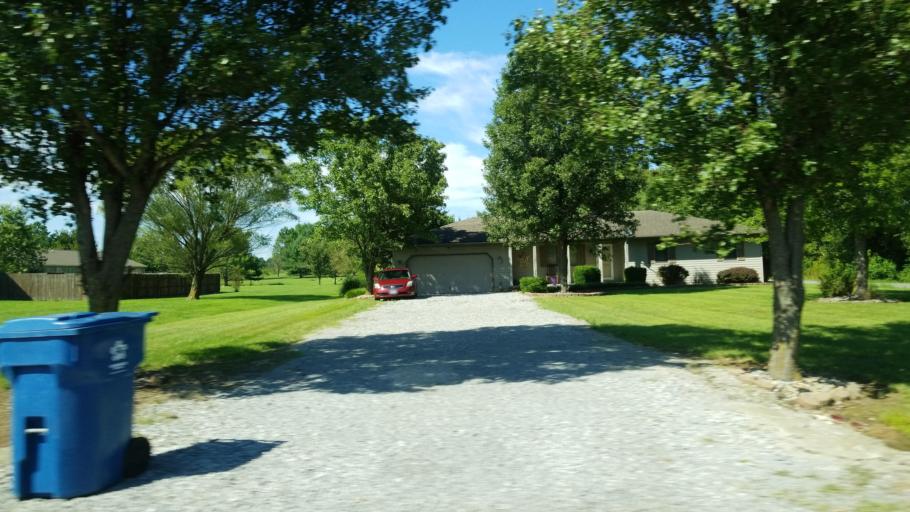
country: US
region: Illinois
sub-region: Williamson County
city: Marion
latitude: 37.7446
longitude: -88.8788
